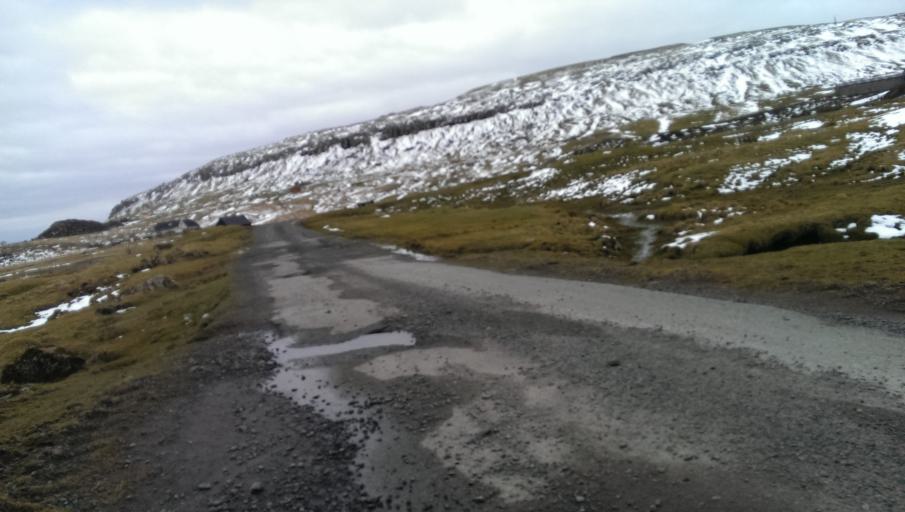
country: FO
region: Streymoy
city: Hoyvik
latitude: 62.0337
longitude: -6.8002
